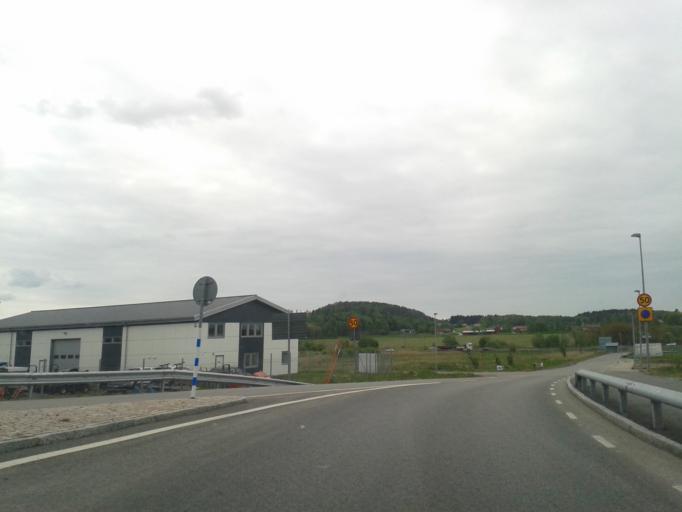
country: SE
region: Vaestra Goetaland
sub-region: Kungalvs Kommun
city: Kungalv
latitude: 57.8976
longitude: 11.9339
